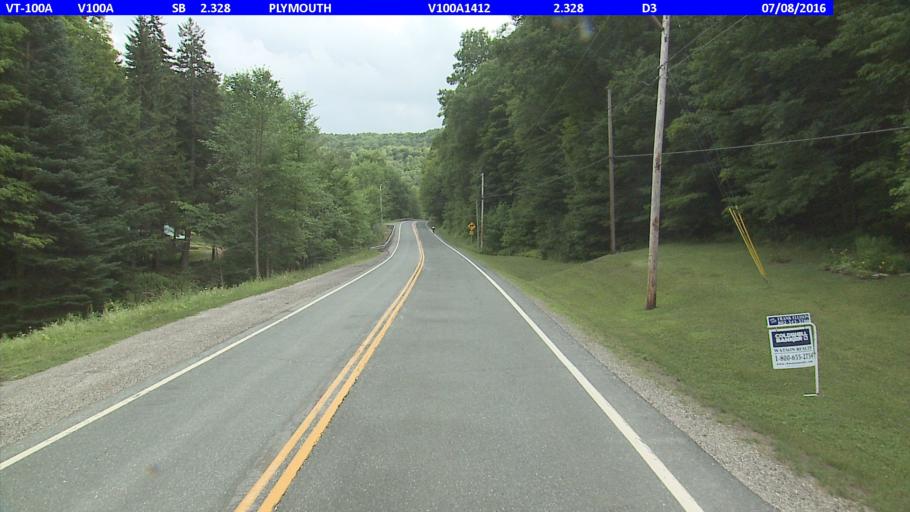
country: US
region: Vermont
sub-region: Windsor County
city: Woodstock
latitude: 43.5484
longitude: -72.7103
